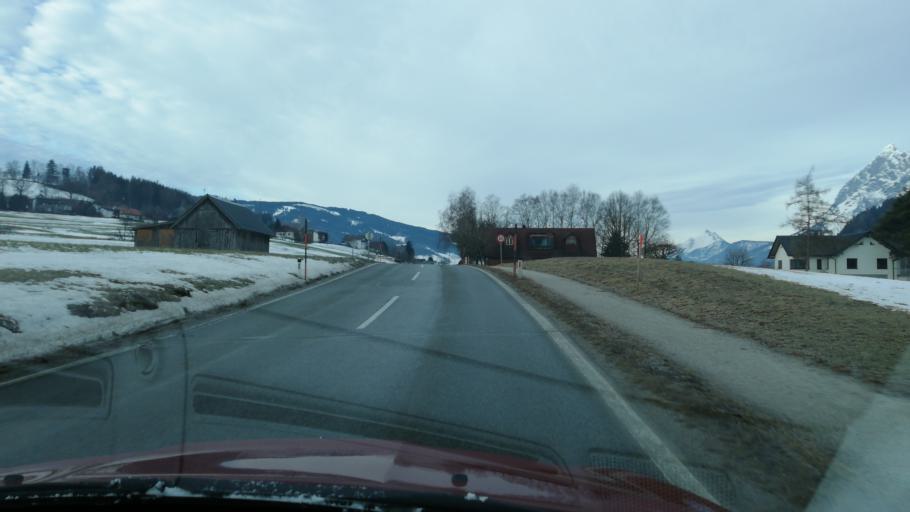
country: AT
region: Styria
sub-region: Politischer Bezirk Liezen
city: Aigen im Ennstal
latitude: 47.5172
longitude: 14.1346
